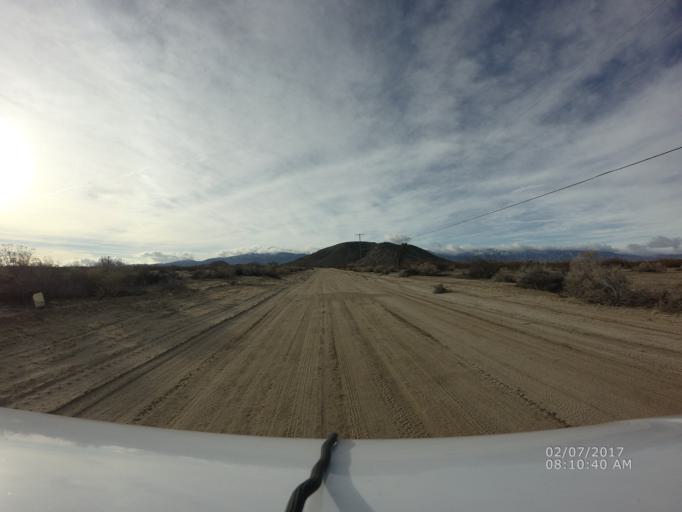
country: US
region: California
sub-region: Los Angeles County
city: Lake Los Angeles
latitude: 34.5749
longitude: -117.7203
